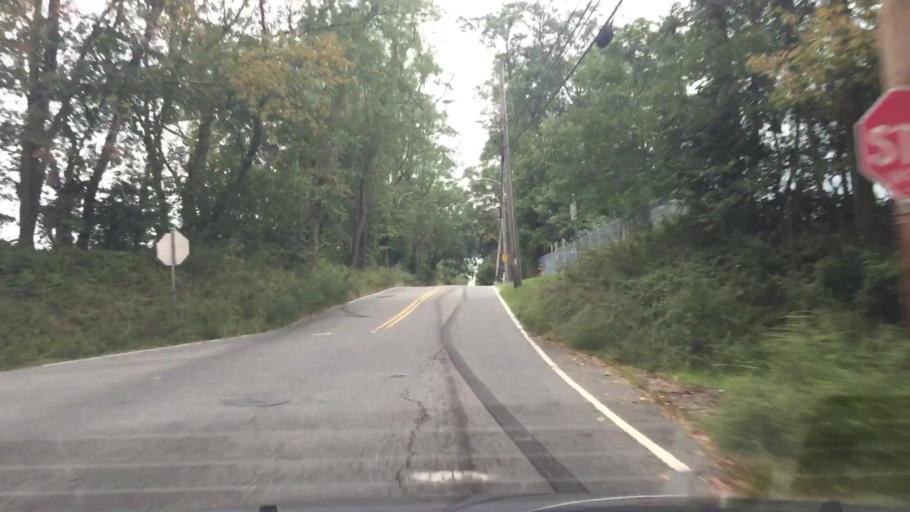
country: US
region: Massachusetts
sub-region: Essex County
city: North Andover
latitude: 42.7267
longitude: -71.1002
